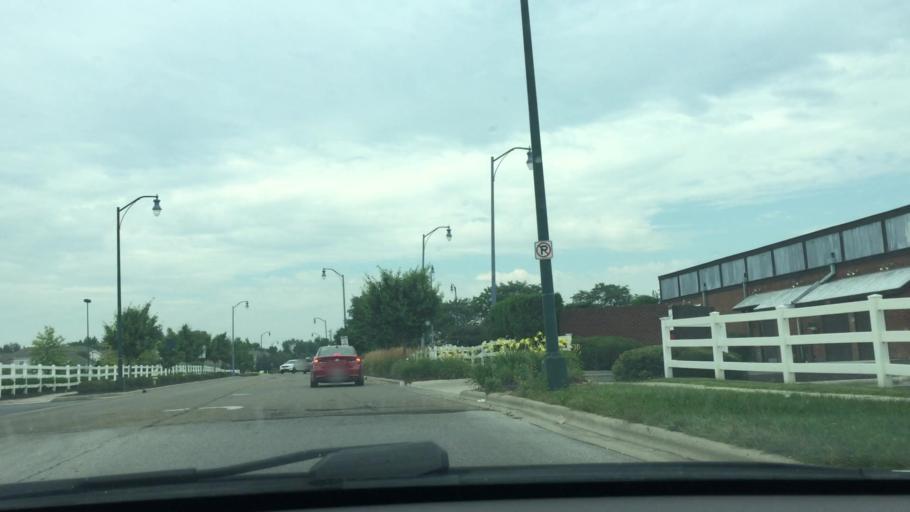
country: US
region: Ohio
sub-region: Franklin County
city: Reynoldsburg
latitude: 39.9356
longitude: -82.7910
